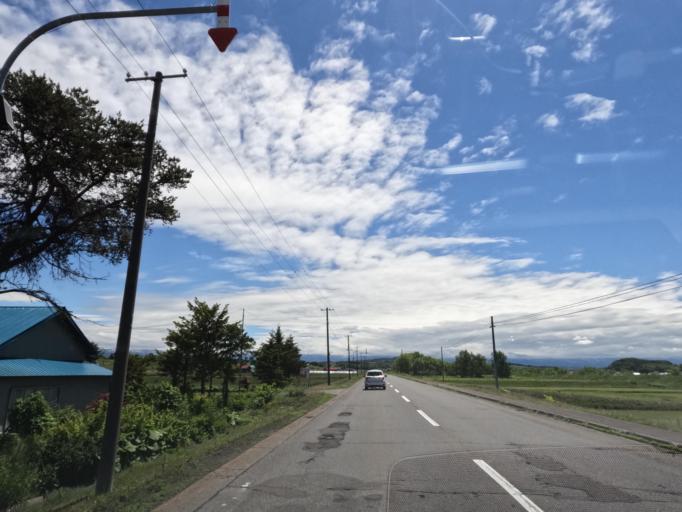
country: JP
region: Hokkaido
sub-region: Asahikawa-shi
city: Asahikawa
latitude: 43.6649
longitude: 142.4229
